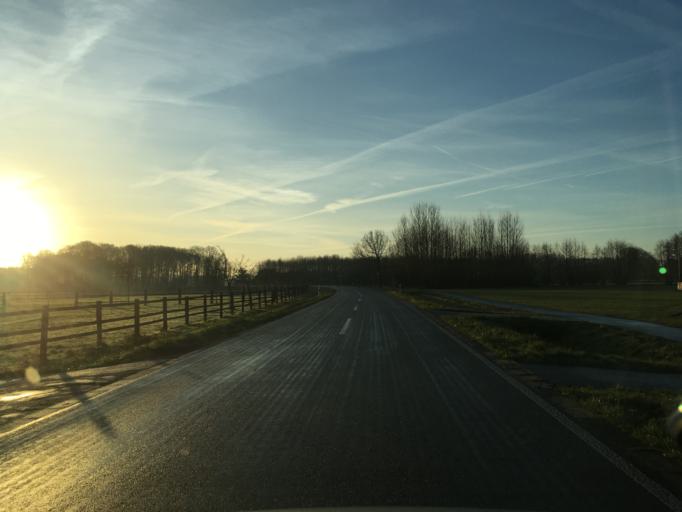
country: DE
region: North Rhine-Westphalia
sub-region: Regierungsbezirk Munster
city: Schoppingen
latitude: 52.0446
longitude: 7.2402
